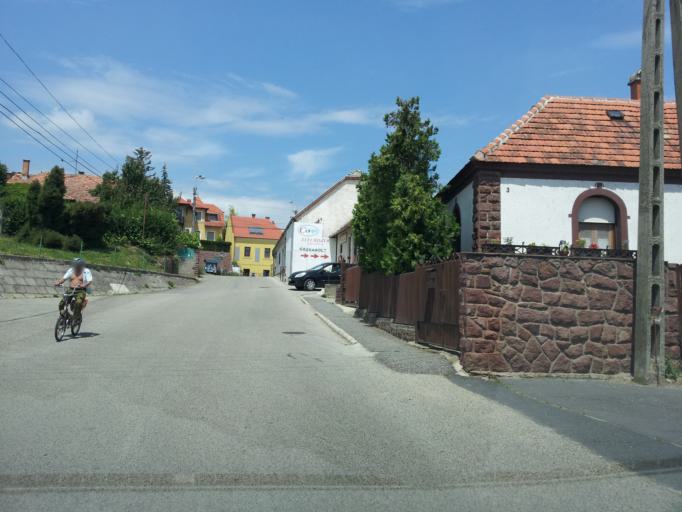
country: HU
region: Veszprem
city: Csopak
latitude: 46.9939
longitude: 17.9742
